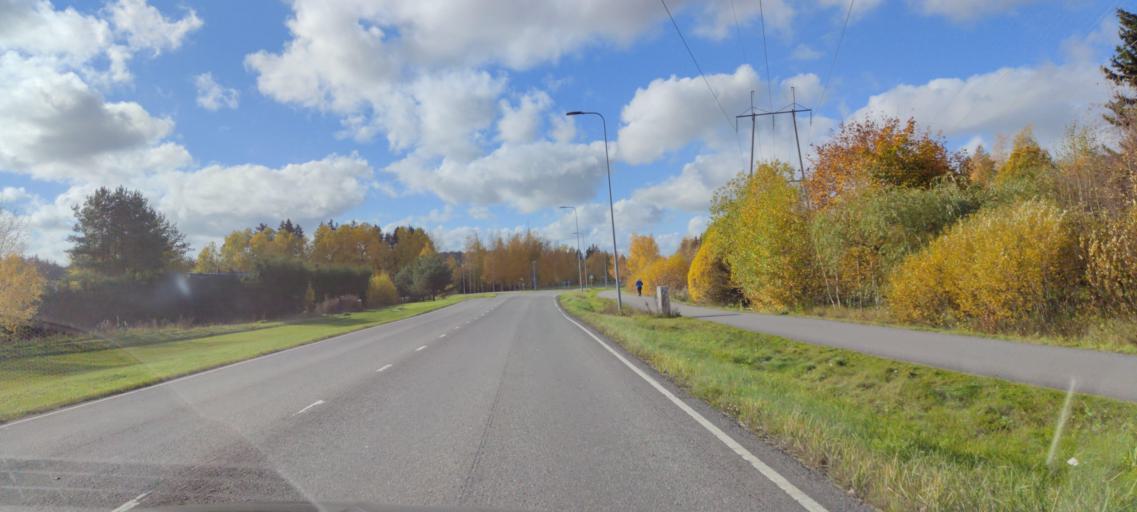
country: FI
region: Varsinais-Suomi
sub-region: Turku
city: Kaarina
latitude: 60.4063
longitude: 22.3336
